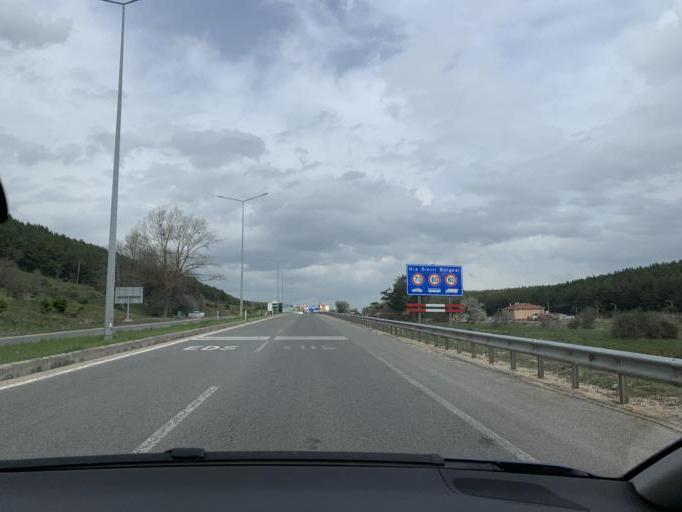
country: TR
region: Bolu
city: Gerede
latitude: 40.7988
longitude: 32.1732
